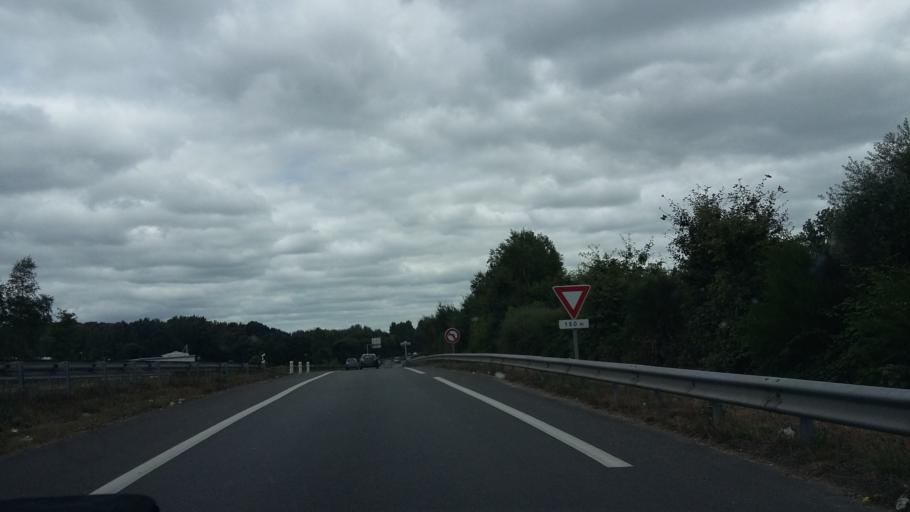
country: FR
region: Pays de la Loire
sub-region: Departement de la Vendee
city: Challans
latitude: 46.8555
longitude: -1.8944
